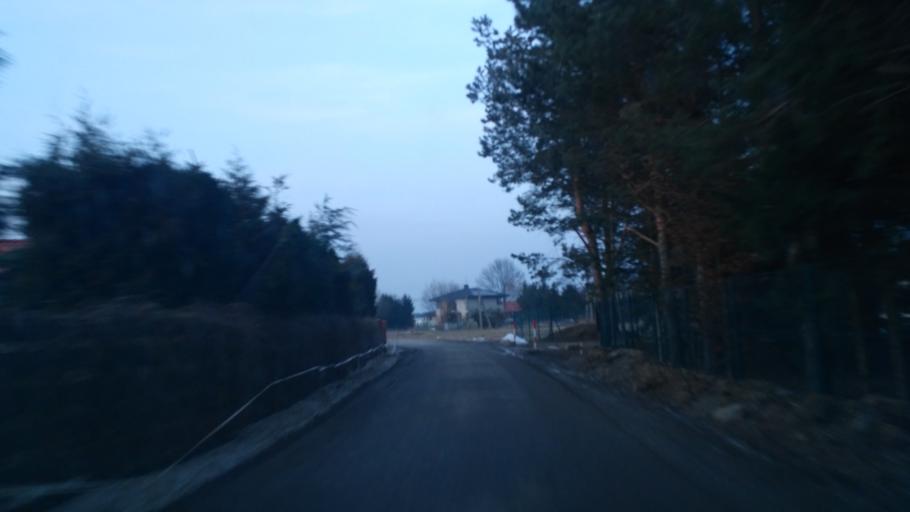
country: PL
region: Subcarpathian Voivodeship
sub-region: Powiat rzeszowski
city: Boguchwala
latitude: 49.9826
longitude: 21.9708
